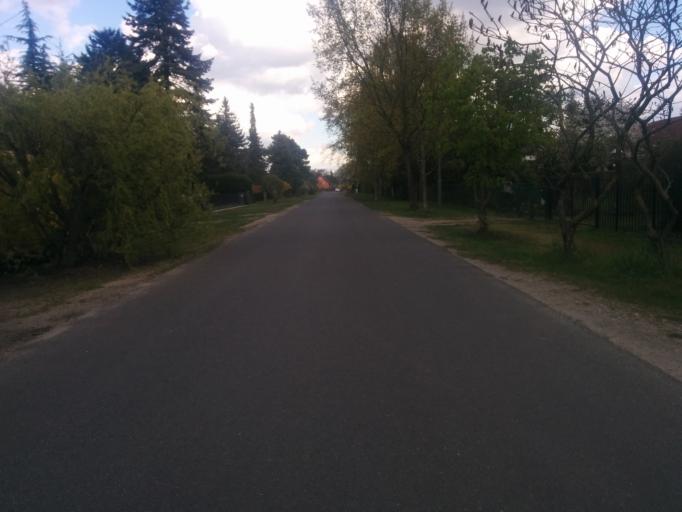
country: DE
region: Berlin
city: Biesdorf
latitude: 52.4946
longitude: 13.5506
